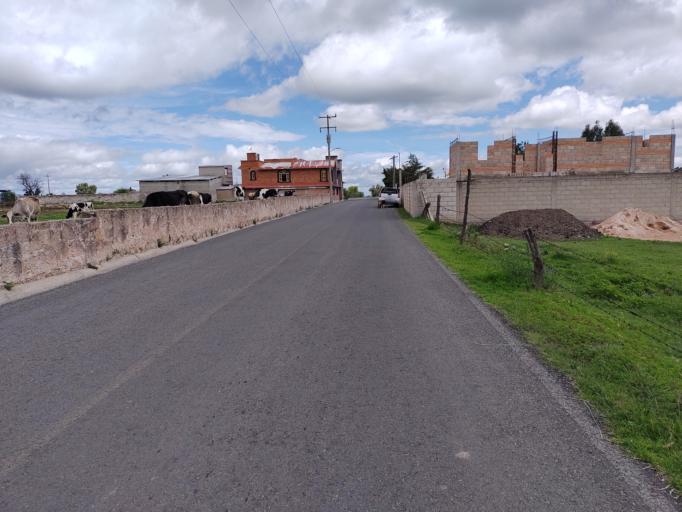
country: MX
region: Mexico
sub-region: Aculco
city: Gunyo Poniente (San Jose Gunyo)
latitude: 20.1177
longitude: -99.8774
